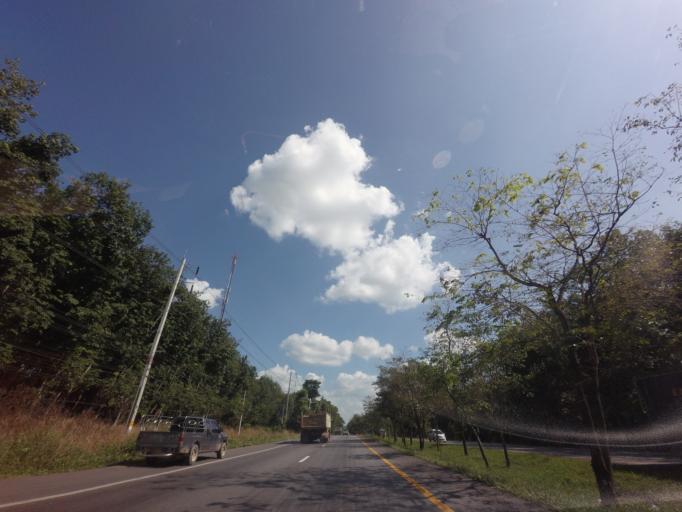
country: TH
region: Rayong
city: Wang Chan
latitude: 12.9501
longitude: 101.5129
